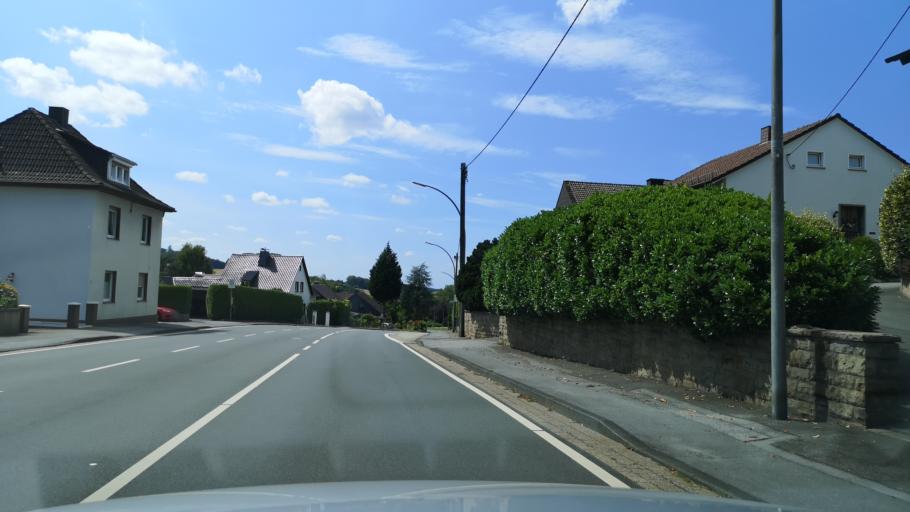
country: DE
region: North Rhine-Westphalia
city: Hemer
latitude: 51.4018
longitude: 7.7469
